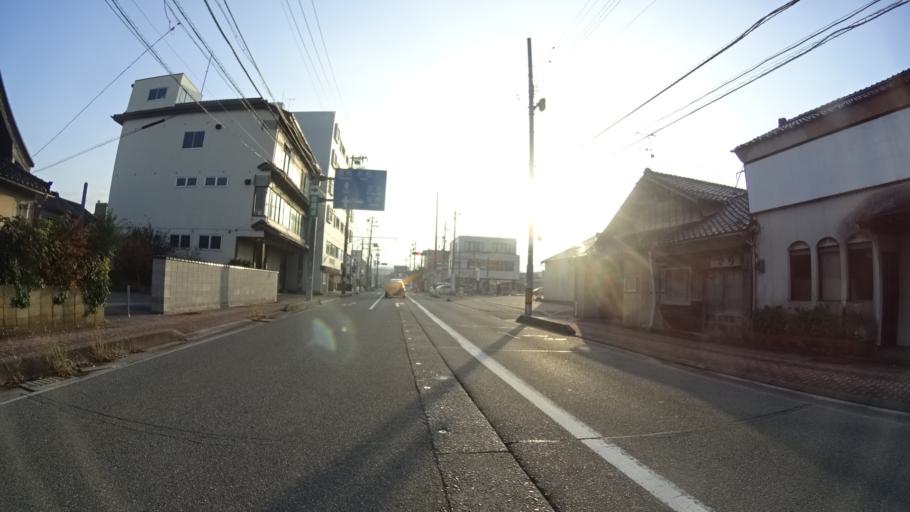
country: JP
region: Ishikawa
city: Nanao
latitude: 37.0421
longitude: 136.9689
